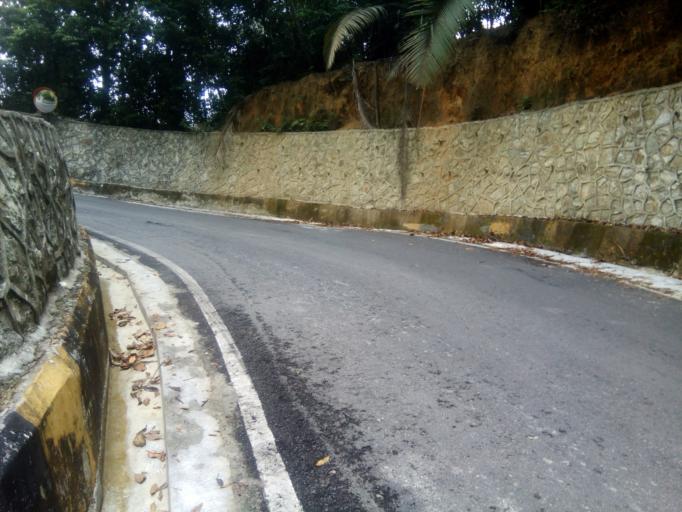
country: MY
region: Penang
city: Tanjung Tokong
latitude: 5.4362
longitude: 100.2843
